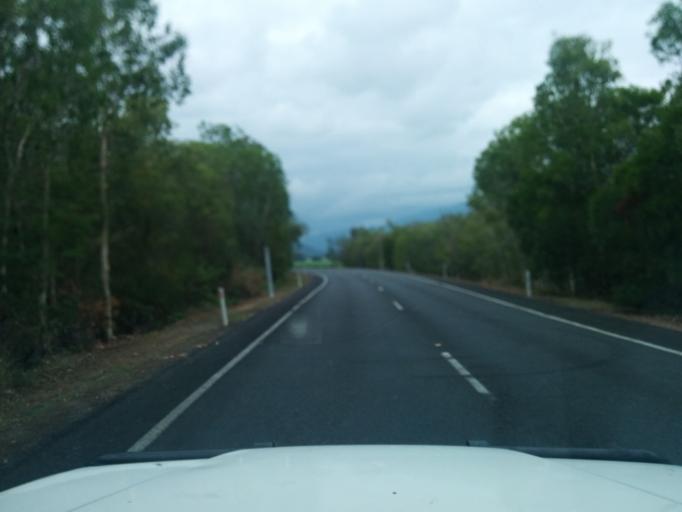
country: AU
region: Queensland
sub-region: Cairns
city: Yorkeys Knob
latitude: -16.8485
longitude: 145.7342
